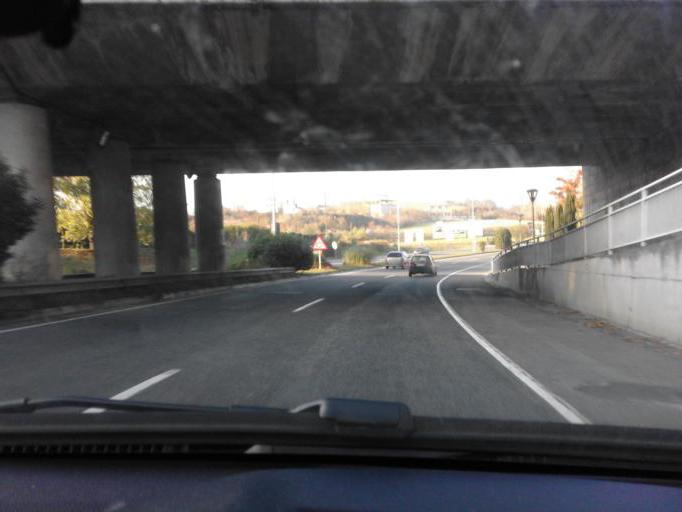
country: ES
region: Navarre
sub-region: Provincia de Navarra
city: Berriozar
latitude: 42.8219
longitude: -1.6709
